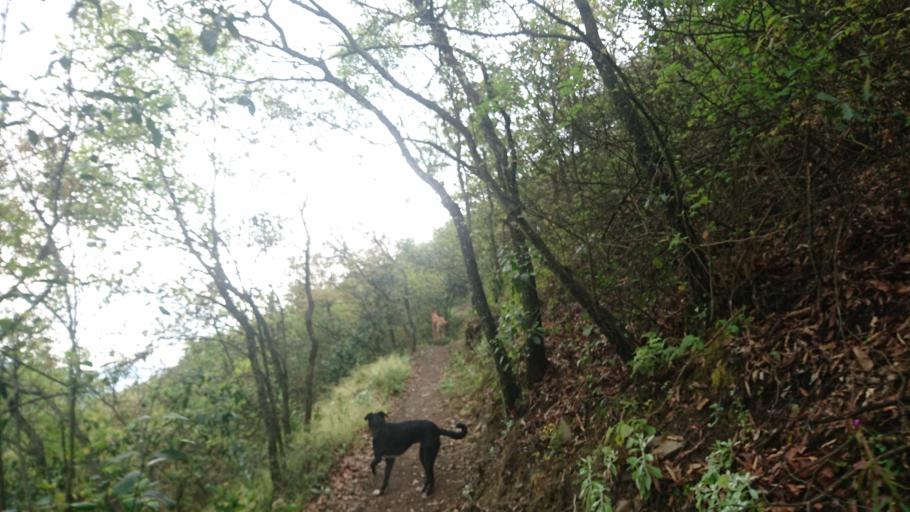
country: MX
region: Nuevo Leon
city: Garza Garcia
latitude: 25.6028
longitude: -100.3376
